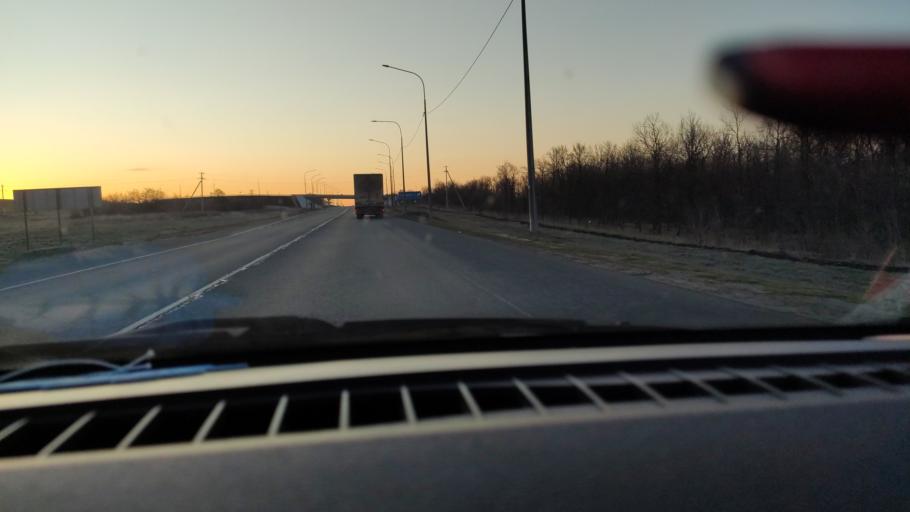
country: RU
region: Saratov
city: Yelshanka
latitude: 51.8258
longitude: 46.2878
